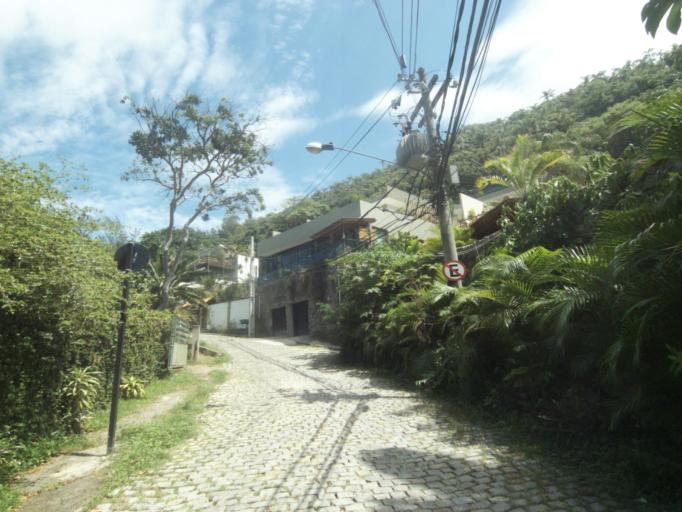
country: BR
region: Rio de Janeiro
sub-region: Niteroi
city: Niteroi
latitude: -22.9734
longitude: -43.0389
